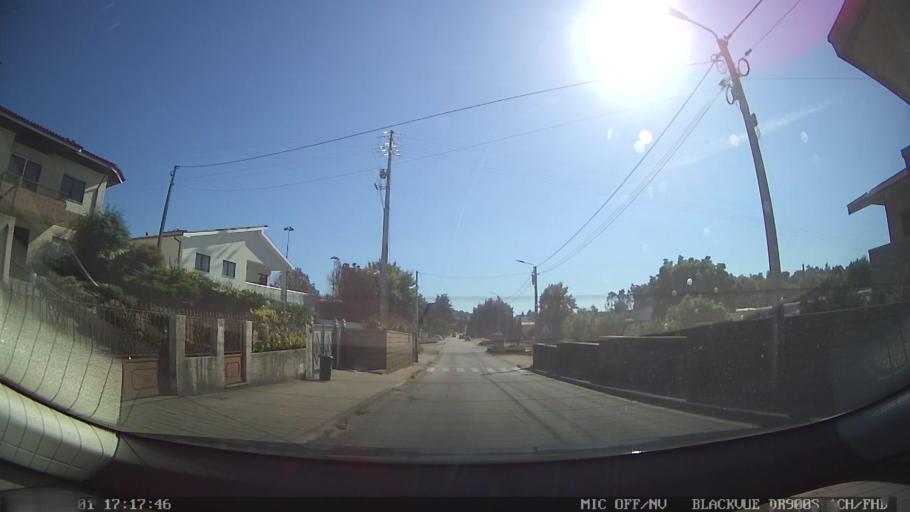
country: PT
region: Porto
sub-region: Santo Tirso
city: Santo Tirso
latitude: 41.3403
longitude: -8.4942
